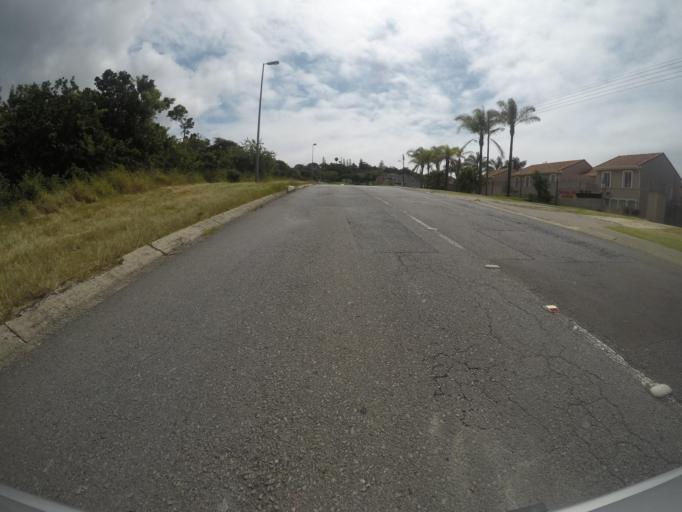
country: ZA
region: Eastern Cape
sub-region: Buffalo City Metropolitan Municipality
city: East London
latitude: -32.9808
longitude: 27.9373
